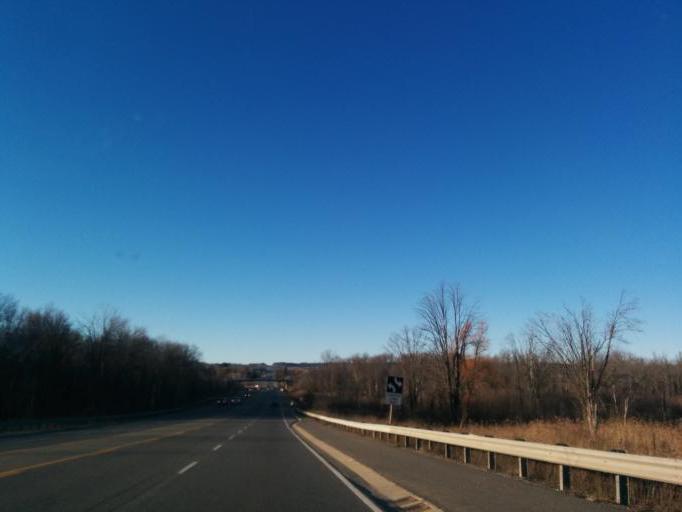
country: CA
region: Ontario
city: Brampton
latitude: 43.8091
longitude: -79.9267
